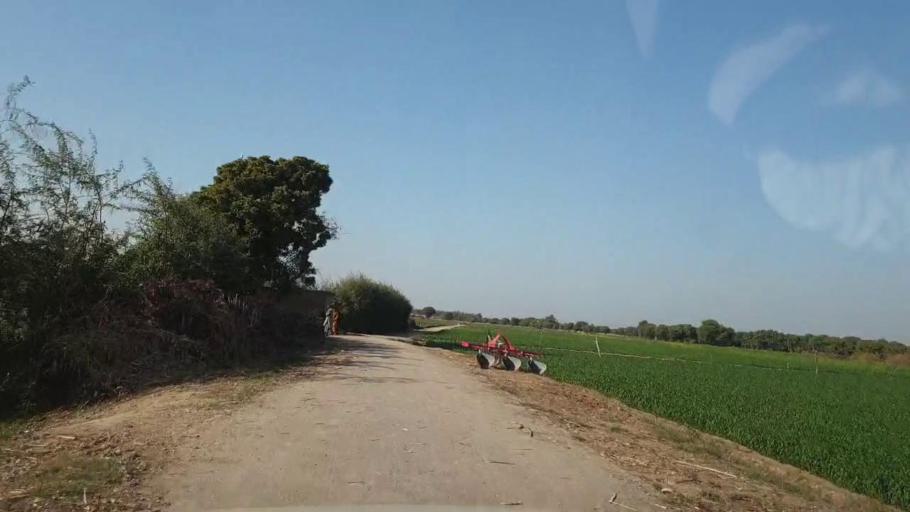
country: PK
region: Sindh
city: Tando Allahyar
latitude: 25.4893
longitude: 68.6503
